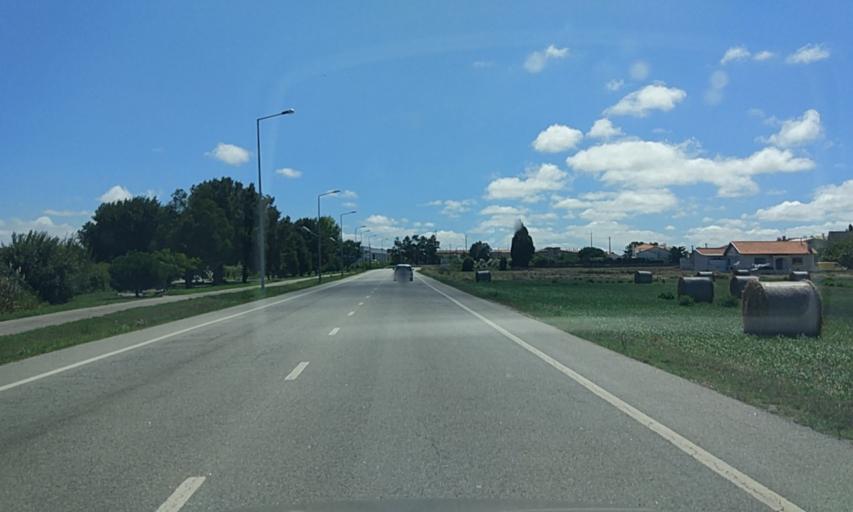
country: PT
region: Aveiro
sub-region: Ilhavo
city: Ilhavo
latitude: 40.6028
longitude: -8.6803
